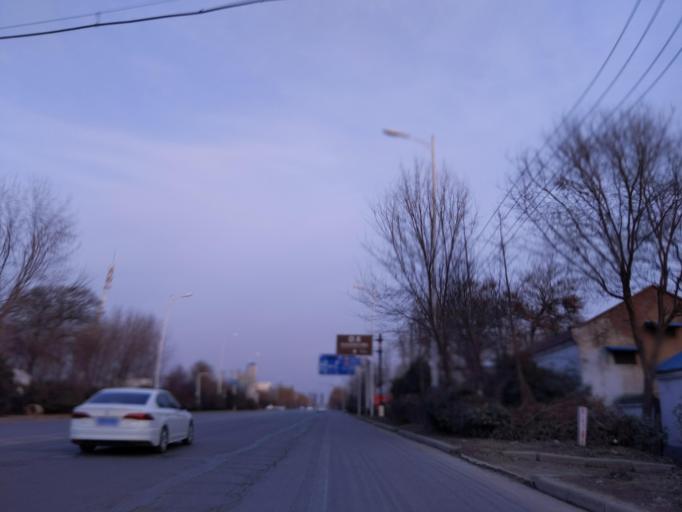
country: CN
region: Henan Sheng
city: Zhongyuanlu
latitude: 35.7869
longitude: 115.1256
